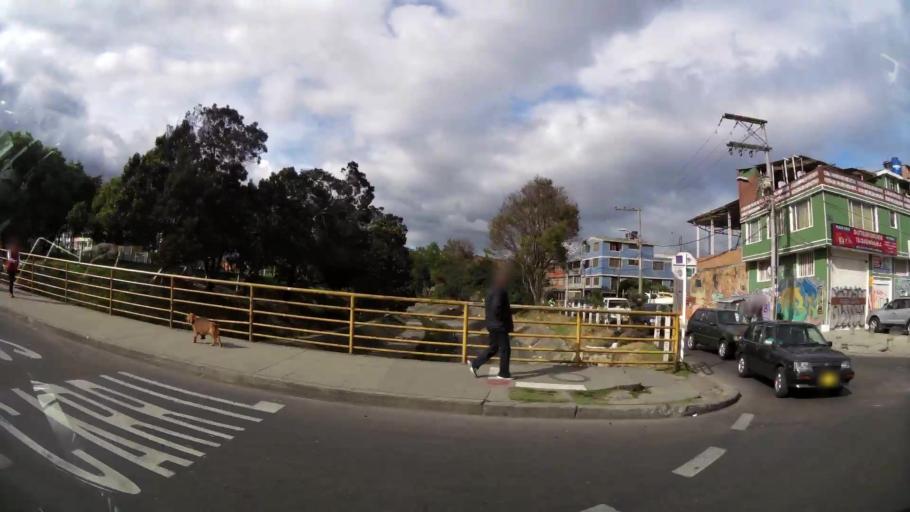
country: CO
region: Bogota D.C.
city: Bogota
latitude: 4.6036
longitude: -74.1225
